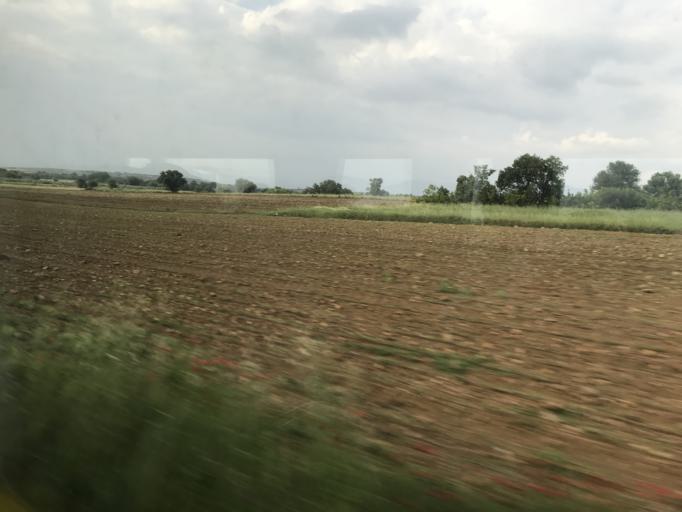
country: GR
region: East Macedonia and Thrace
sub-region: Nomos Rodopis
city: Sapes
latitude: 41.0349
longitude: 25.6729
